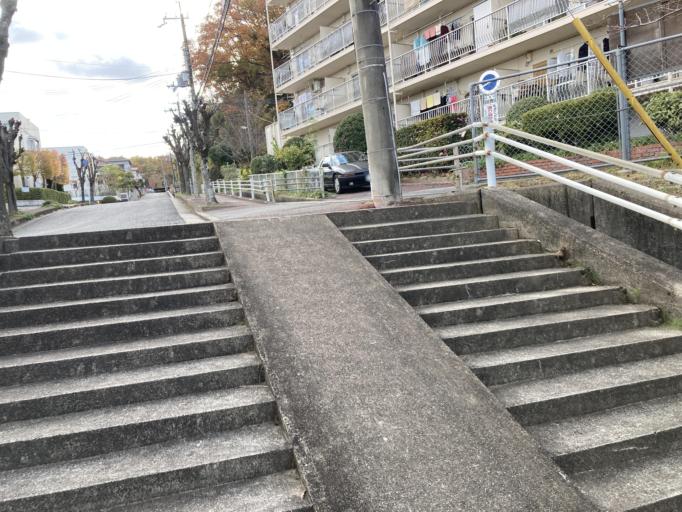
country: JP
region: Nara
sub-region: Ikoma-shi
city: Ikoma
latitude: 34.6876
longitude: 135.7247
